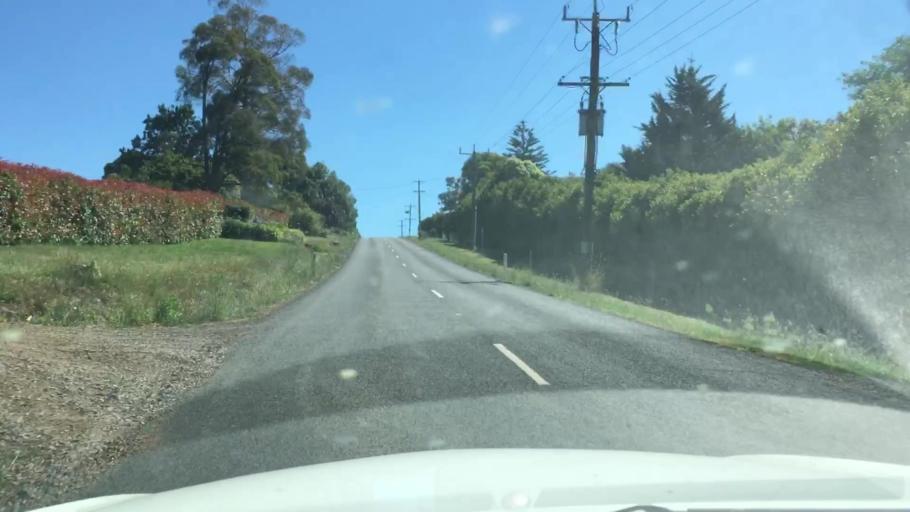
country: AU
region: Victoria
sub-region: Yarra Ranges
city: Mount Evelyn
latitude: -37.8075
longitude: 145.4337
